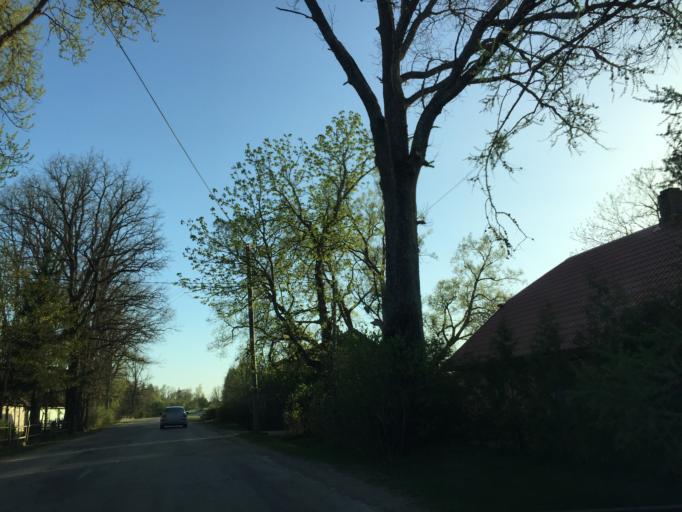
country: LV
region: Koknese
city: Koknese
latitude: 56.6737
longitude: 25.4756
